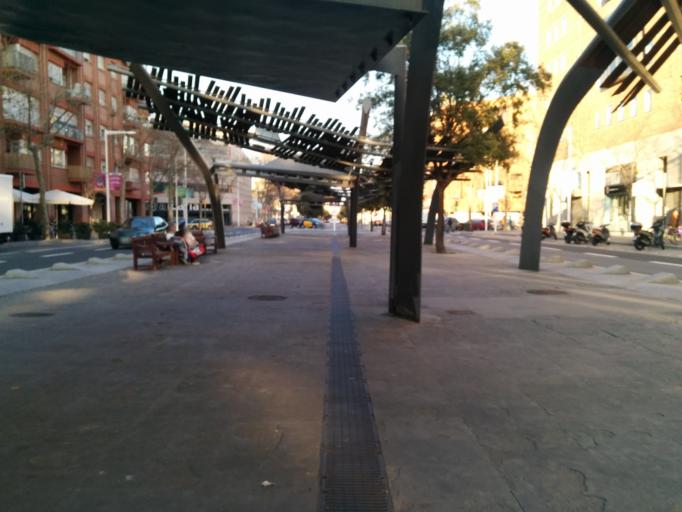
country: ES
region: Catalonia
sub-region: Provincia de Barcelona
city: Ciutat Vella
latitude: 41.3912
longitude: 2.1971
